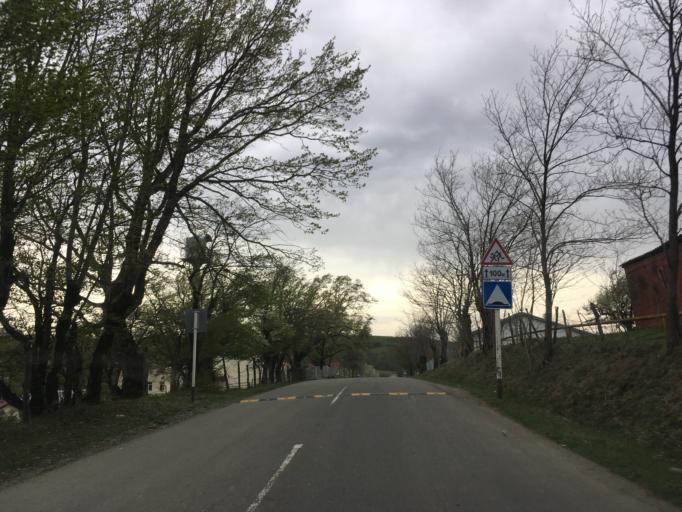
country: GE
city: Surami
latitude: 42.2120
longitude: 43.4211
